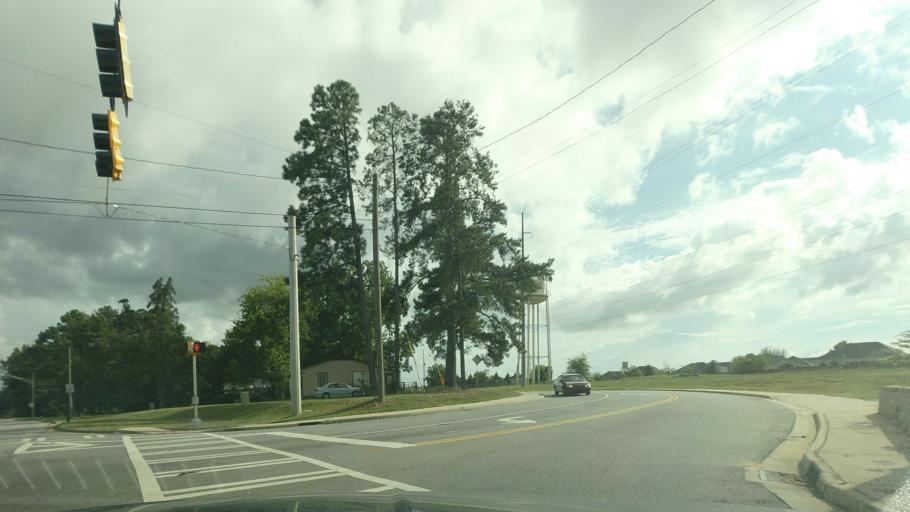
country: US
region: Georgia
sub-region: Houston County
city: Centerville
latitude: 32.6266
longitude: -83.6895
